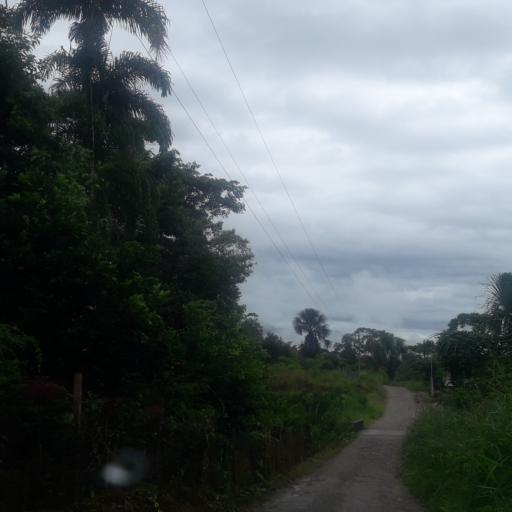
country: EC
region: Napo
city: Archidona
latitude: -0.9203
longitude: -77.8193
